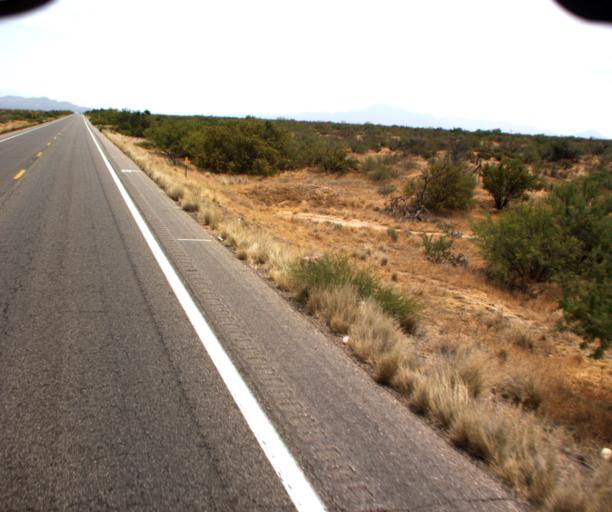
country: US
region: Arizona
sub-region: Gila County
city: Peridot
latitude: 33.3168
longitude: -110.5250
